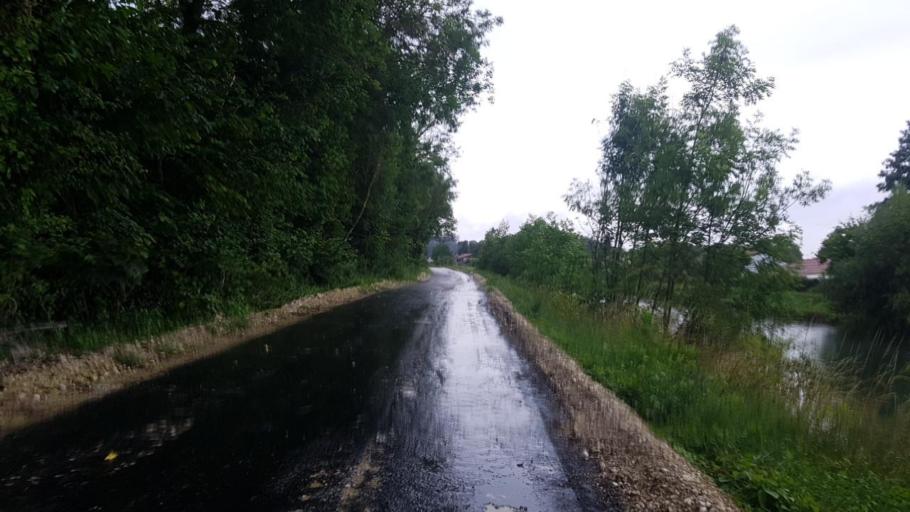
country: FR
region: Champagne-Ardenne
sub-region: Departement de la Marne
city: Sarry
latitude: 48.8589
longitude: 4.4786
